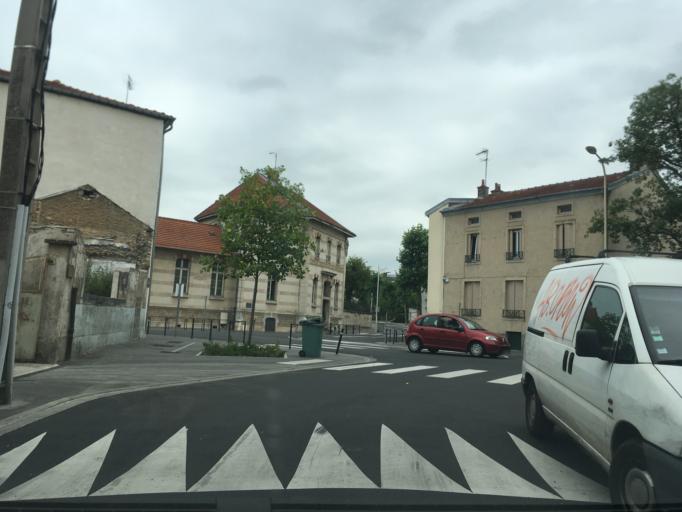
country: FR
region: Lorraine
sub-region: Departement de Meurthe-et-Moselle
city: Nancy
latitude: 48.6983
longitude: 6.1923
